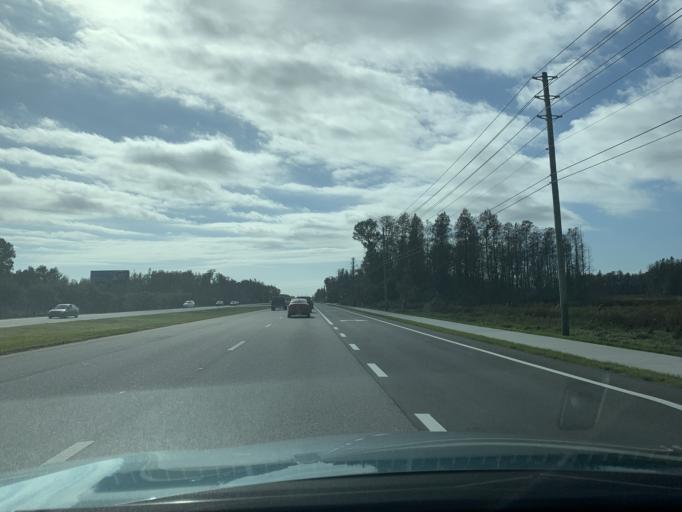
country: US
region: Florida
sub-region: Pasco County
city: Trinity
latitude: 28.1993
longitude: -82.6667
